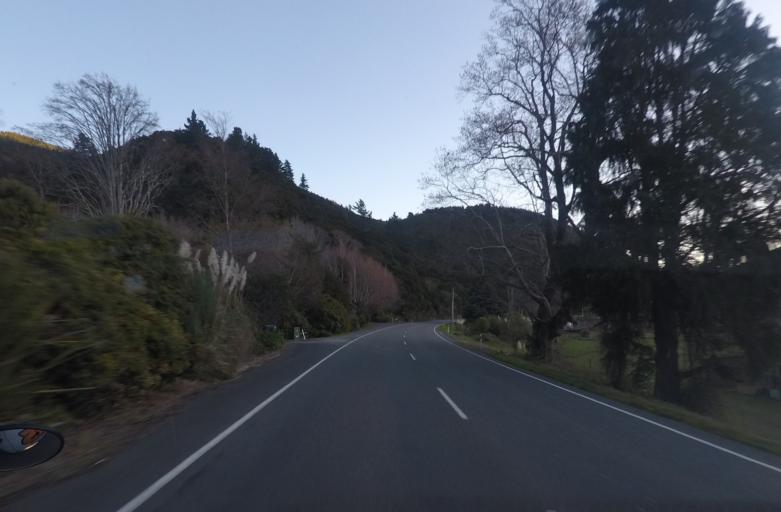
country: NZ
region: Marlborough
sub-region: Marlborough District
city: Picton
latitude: -41.2746
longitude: 173.7434
